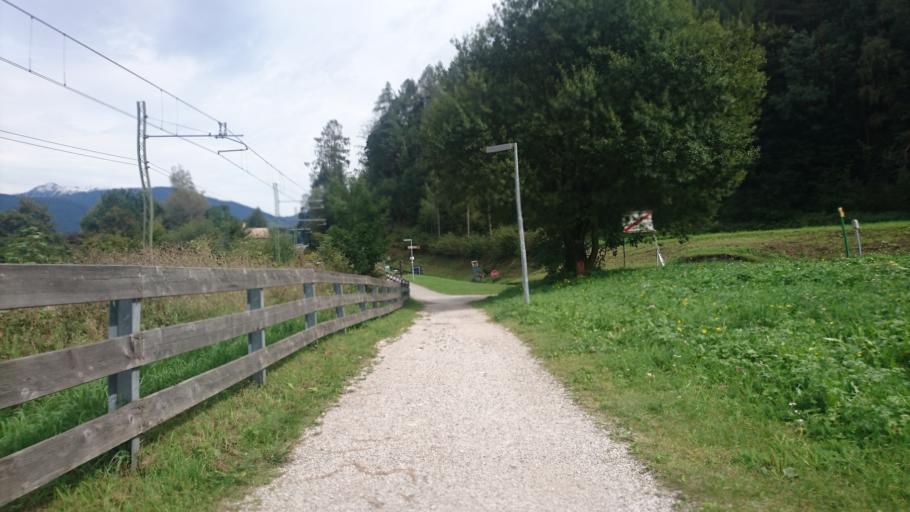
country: IT
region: Trentino-Alto Adige
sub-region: Bolzano
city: San Lorenzo di Sebato
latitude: 46.7811
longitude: 11.9048
